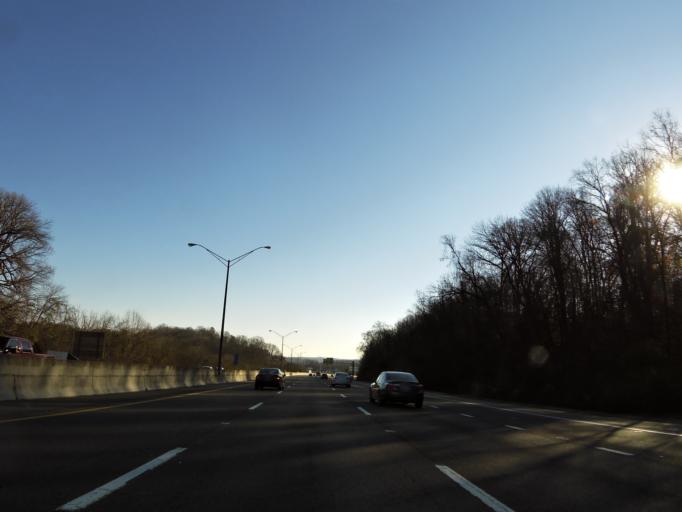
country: US
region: Tennessee
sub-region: Knox County
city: Knoxville
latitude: 36.0120
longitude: -83.8482
